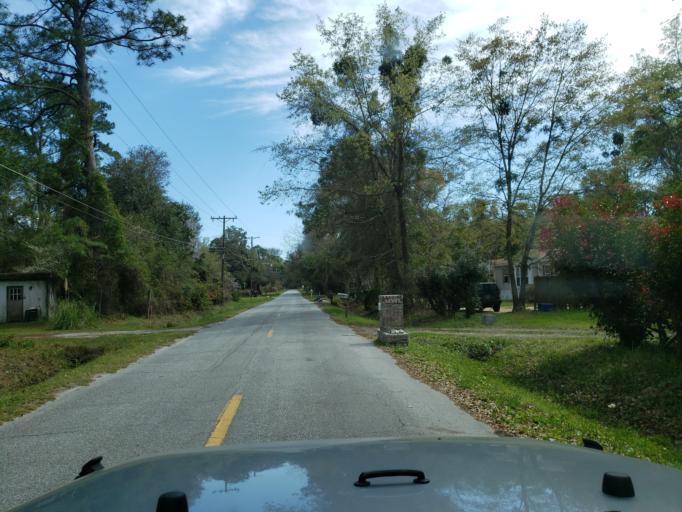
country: US
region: Georgia
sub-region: Chatham County
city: Montgomery
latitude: 31.9508
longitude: -81.1137
